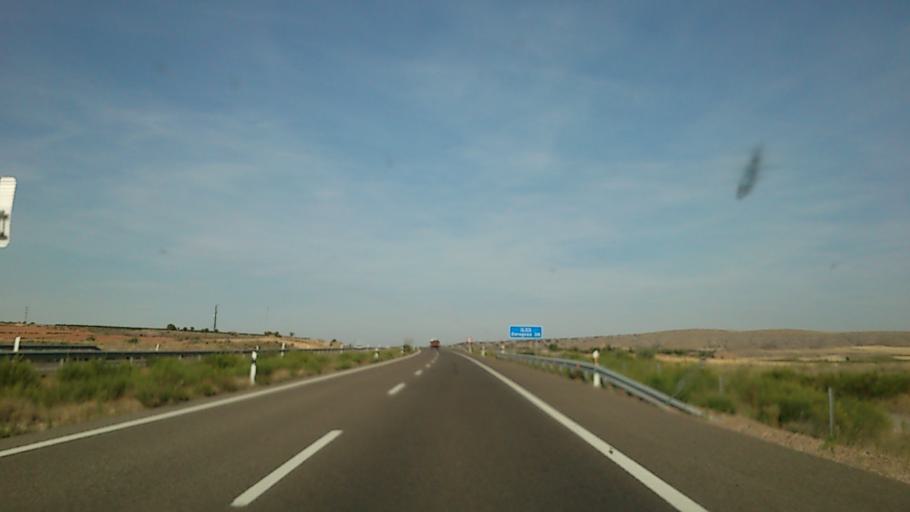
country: ES
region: Aragon
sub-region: Provincia de Zaragoza
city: Longares
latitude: 41.4137
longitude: -1.1655
